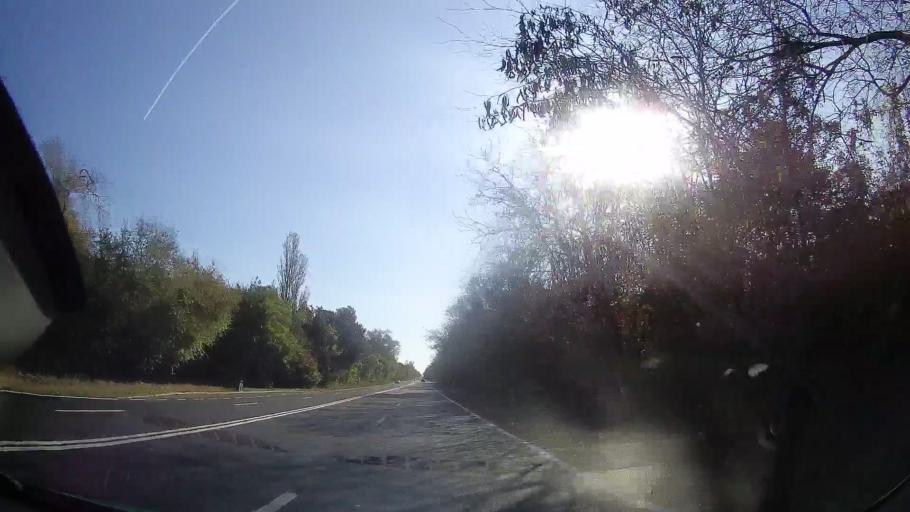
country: RO
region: Constanta
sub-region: Comuna Douazeci si Trei August
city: Dulcesti
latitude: 43.8775
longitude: 28.5738
